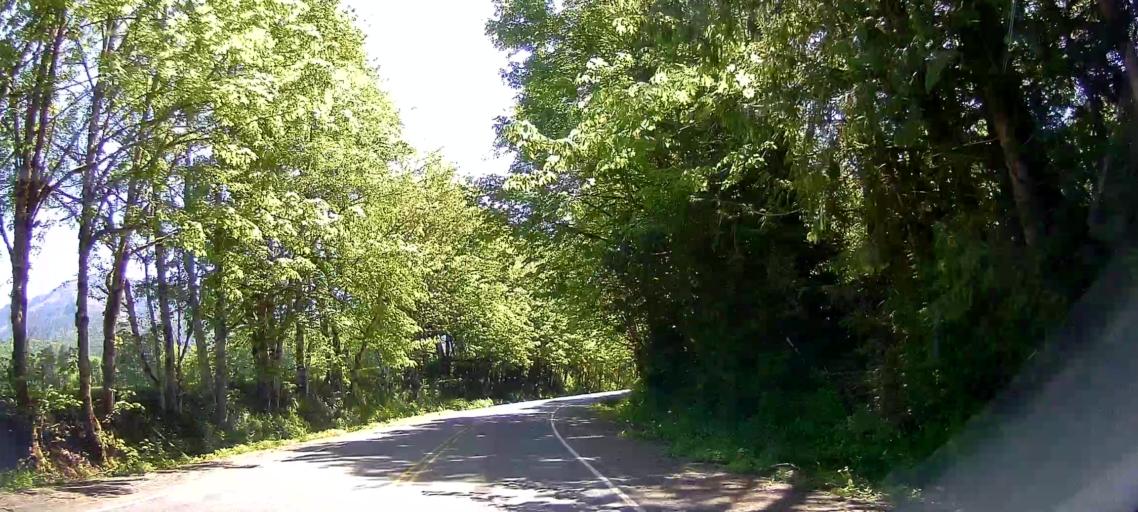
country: US
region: Washington
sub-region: Snohomish County
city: Darrington
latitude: 48.5195
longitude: -121.7279
